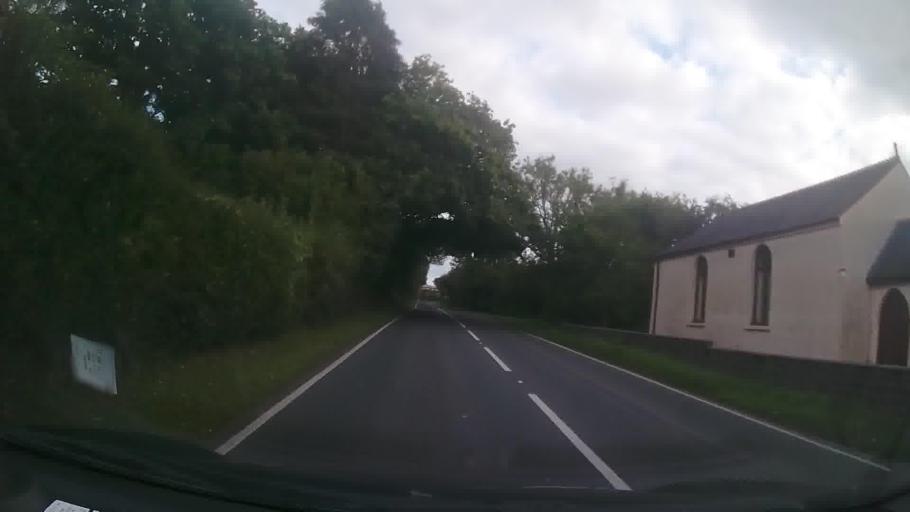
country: GB
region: Wales
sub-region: Pembrokeshire
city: Kilgetty
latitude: 51.7107
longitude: -4.7300
